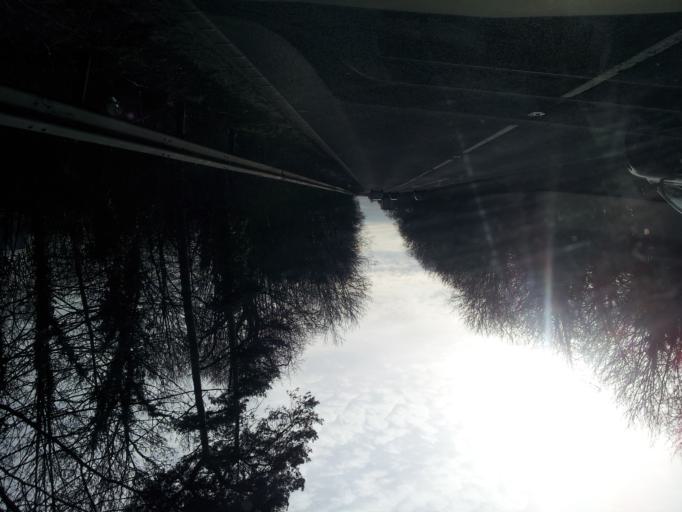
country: GB
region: England
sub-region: Peterborough
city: Castor
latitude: 52.5501
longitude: -0.3370
